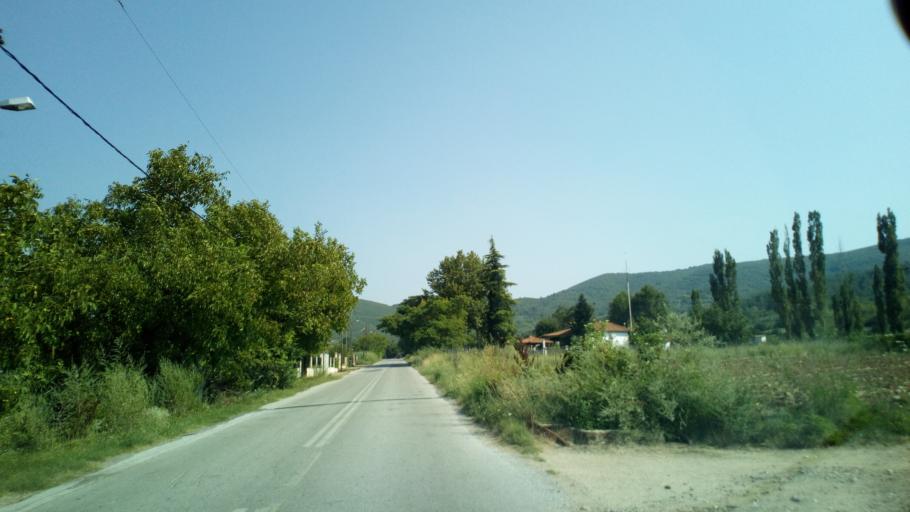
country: GR
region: Central Macedonia
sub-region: Nomos Chalkidikis
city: Galatista
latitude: 40.5600
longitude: 23.2969
